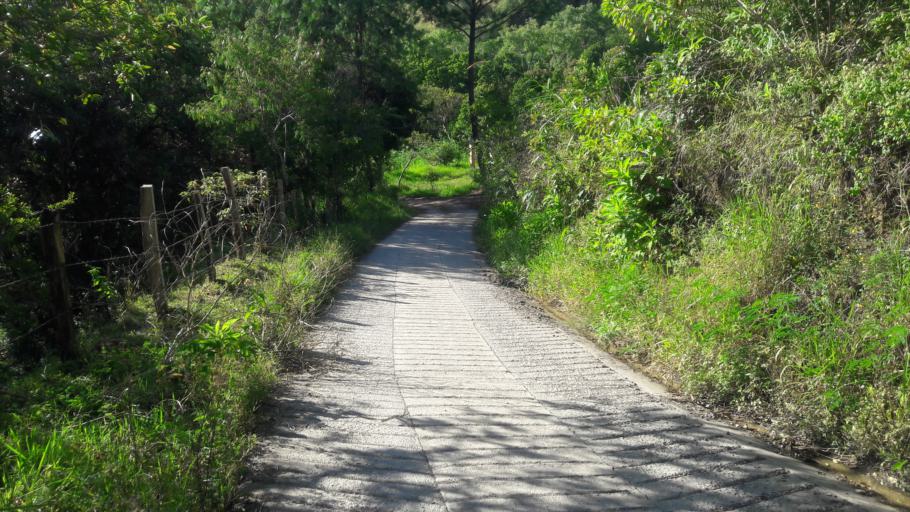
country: CO
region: Cundinamarca
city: Tenza
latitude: 5.0868
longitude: -73.4180
